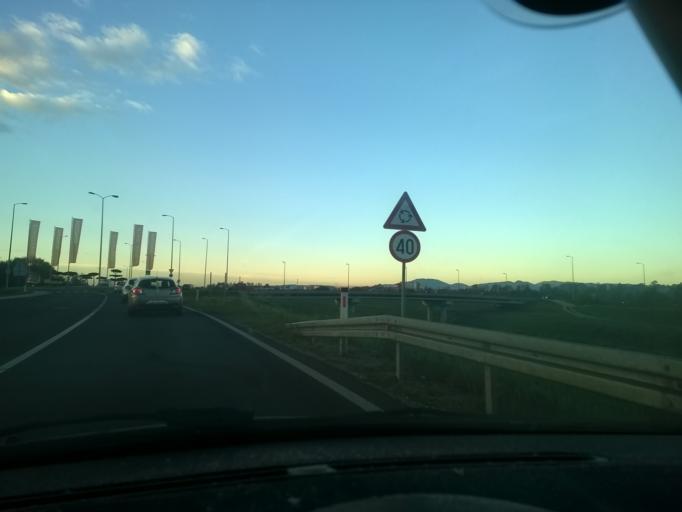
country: HR
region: Zagrebacka
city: Zapresic
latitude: 45.8793
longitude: 15.8195
